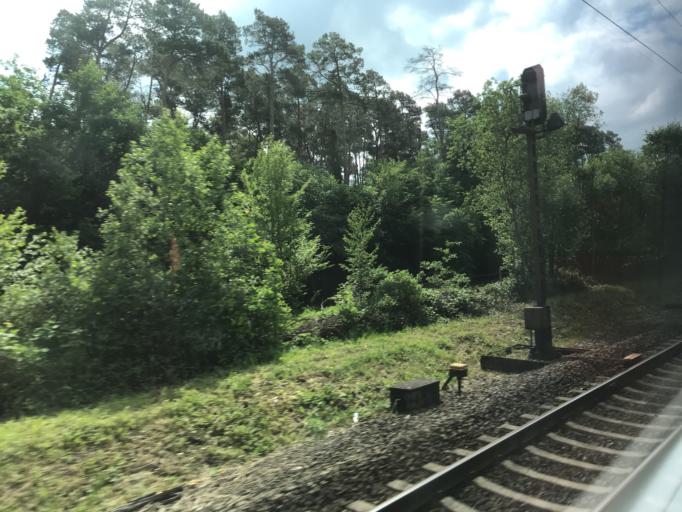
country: DE
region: Baden-Wuerttemberg
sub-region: Tuebingen Region
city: Westerstetten
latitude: 48.5165
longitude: 9.9507
